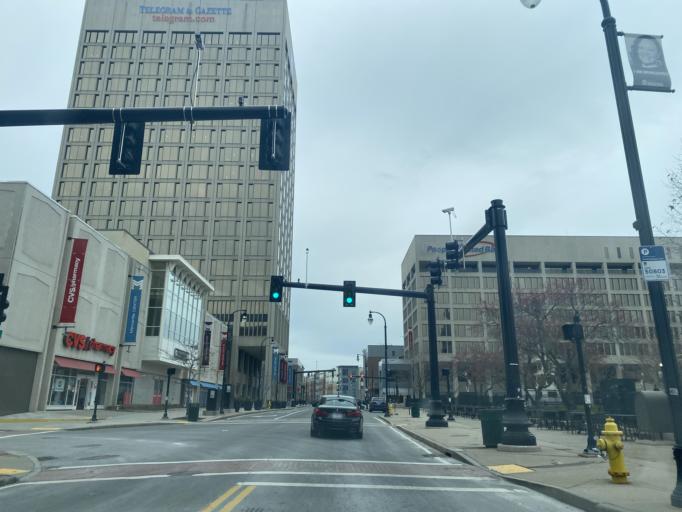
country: US
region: Massachusetts
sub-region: Worcester County
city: Worcester
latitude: 42.2628
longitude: -71.8008
